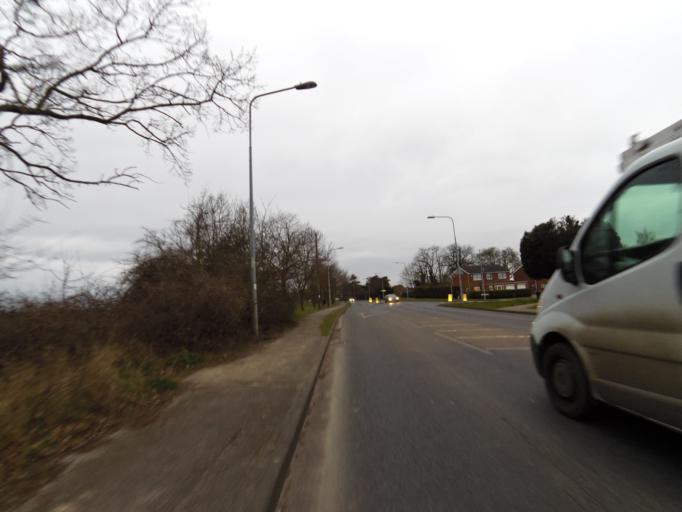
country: GB
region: England
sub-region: Suffolk
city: Ipswich
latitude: 52.0847
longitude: 1.1492
